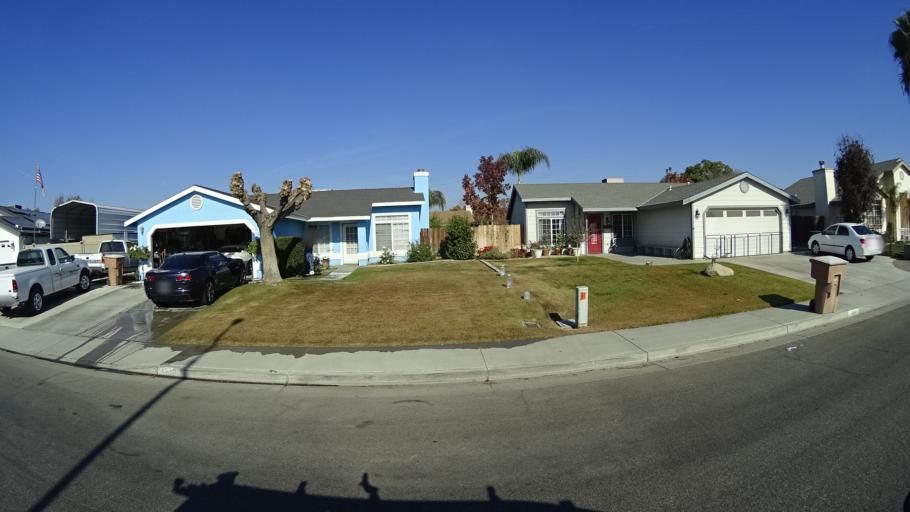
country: US
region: California
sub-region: Kern County
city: Greenfield
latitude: 35.2900
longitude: -119.0509
